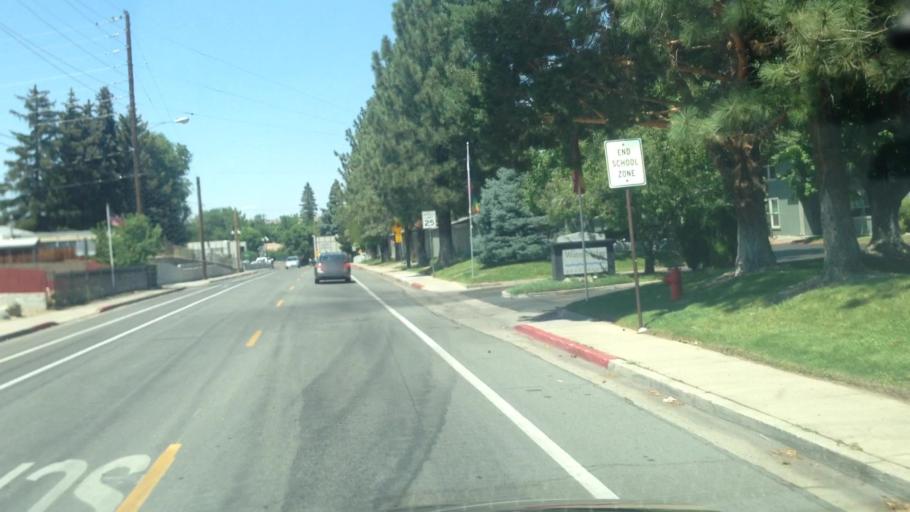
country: US
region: Nevada
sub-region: Washoe County
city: Reno
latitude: 39.5187
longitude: -119.8264
